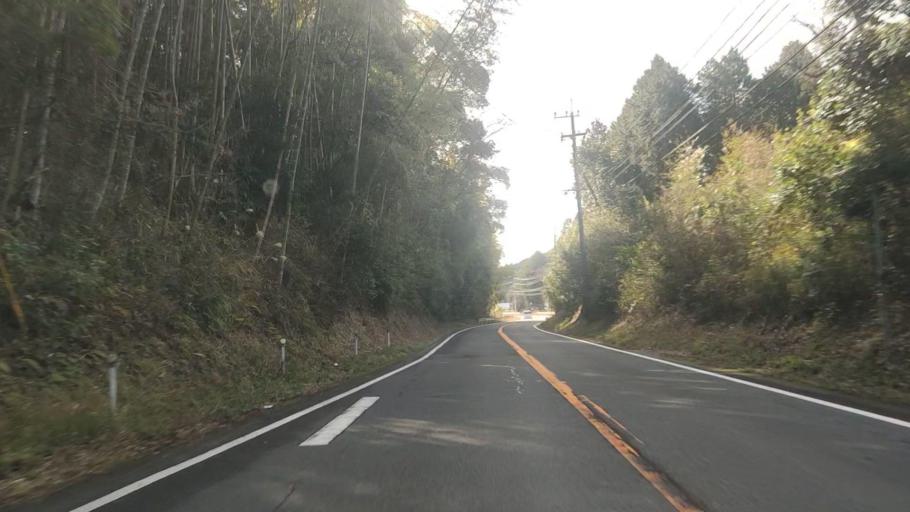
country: JP
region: Kagoshima
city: Okuchi-shinohara
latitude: 31.9282
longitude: 130.7031
